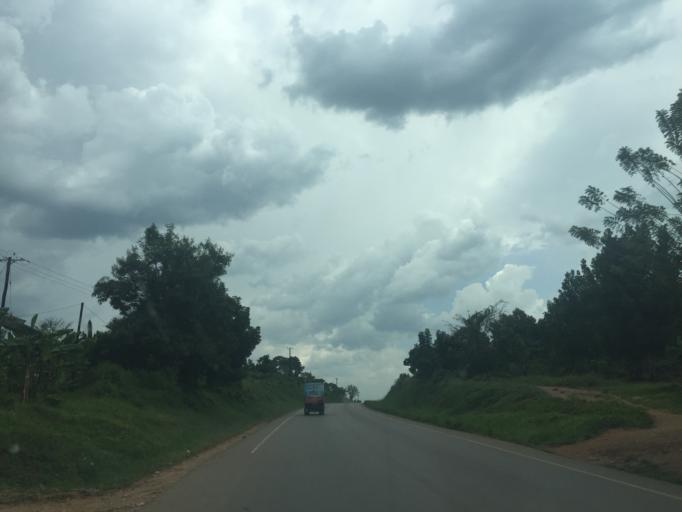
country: UG
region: Central Region
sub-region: Luwero District
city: Wobulenzi
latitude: 0.6735
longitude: 32.5282
